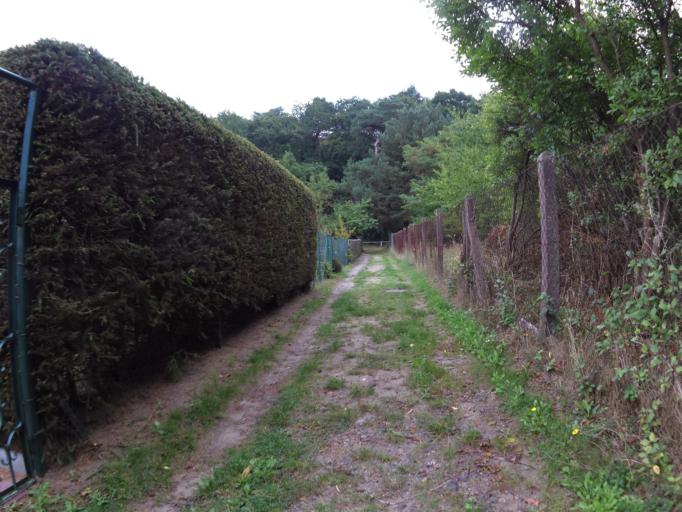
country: DE
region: Mecklenburg-Vorpommern
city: Seebad Heringsdorf
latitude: 53.9215
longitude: 14.1636
